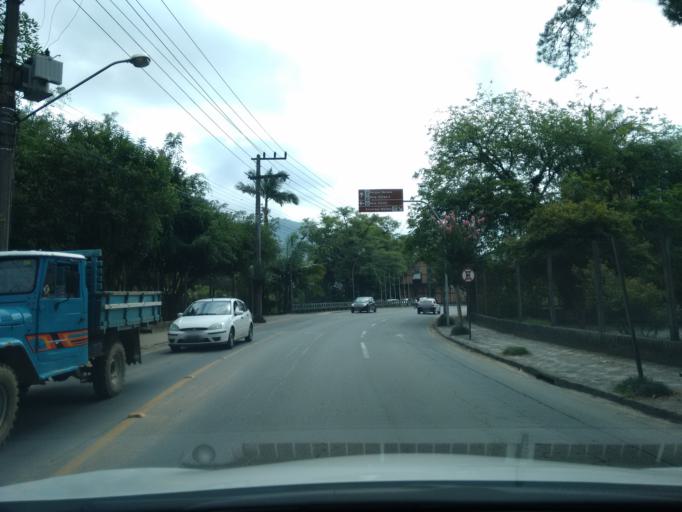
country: BR
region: Santa Catarina
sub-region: Jaragua Do Sul
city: Jaragua do Sul
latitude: -26.5138
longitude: -49.1251
